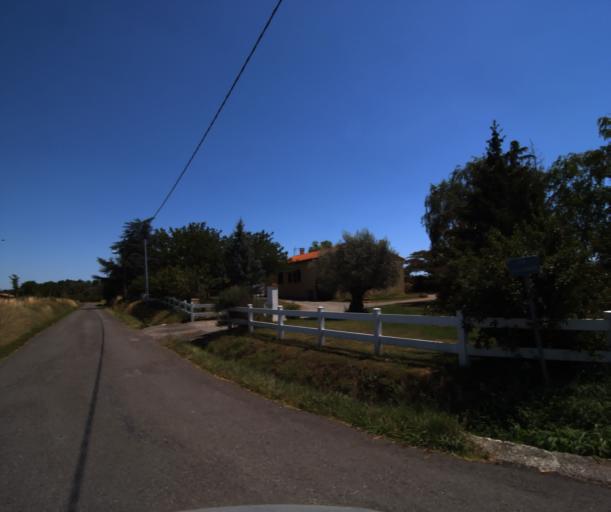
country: FR
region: Midi-Pyrenees
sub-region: Departement de la Haute-Garonne
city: Le Fauga
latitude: 43.4377
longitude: 1.2875
